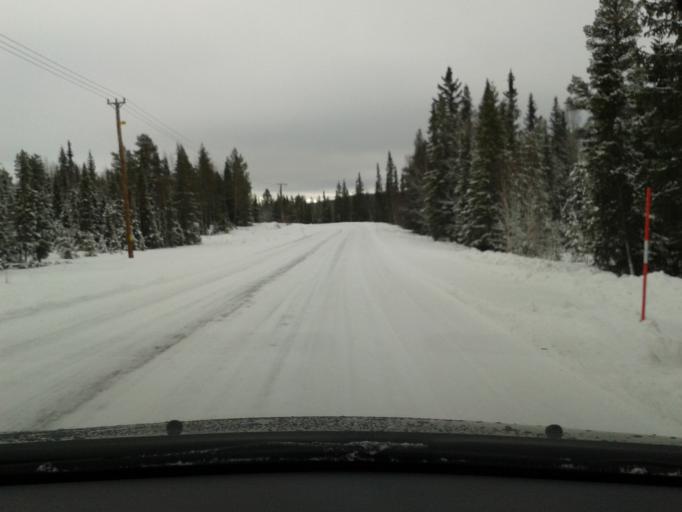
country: SE
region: Vaesterbotten
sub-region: Vilhelmina Kommun
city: Sjoberg
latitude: 65.2261
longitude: 15.9219
